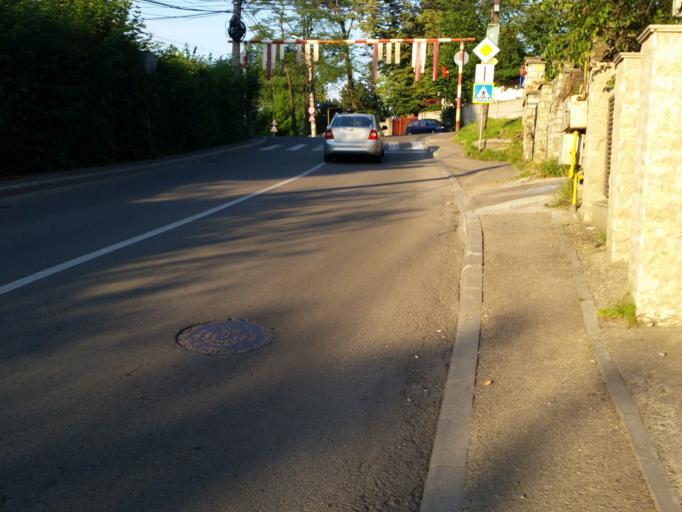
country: RO
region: Cluj
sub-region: Municipiul Cluj-Napoca
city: Cluj-Napoca
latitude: 46.7758
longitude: 23.5732
